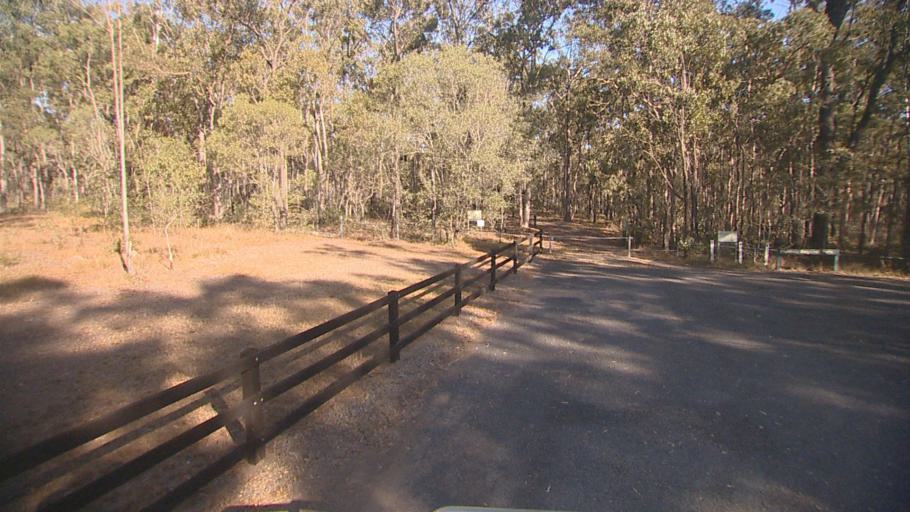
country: AU
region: Queensland
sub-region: Gold Coast
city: Ormeau Hills
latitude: -27.8268
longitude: 153.1679
